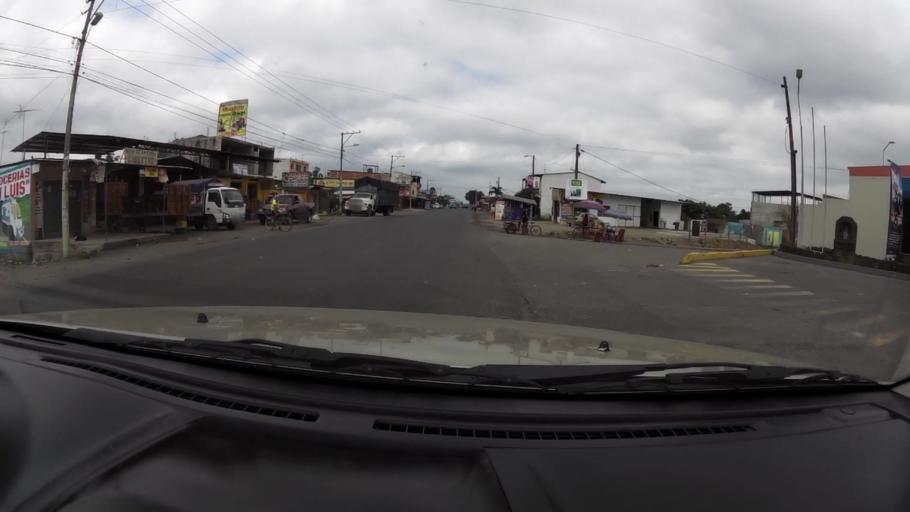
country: EC
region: Guayas
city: Naranjal
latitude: -2.6831
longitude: -79.6240
